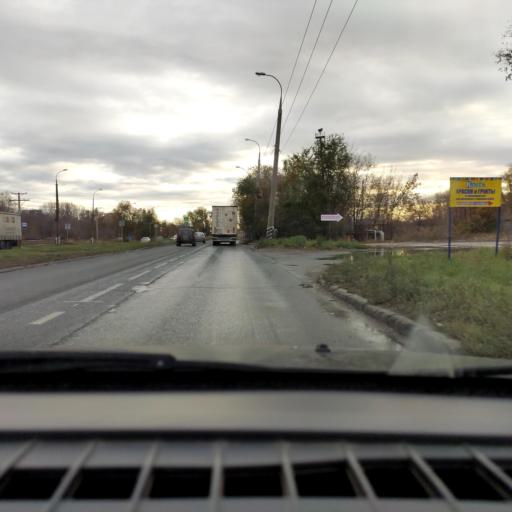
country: RU
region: Samara
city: Tol'yatti
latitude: 53.5587
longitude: 49.3166
